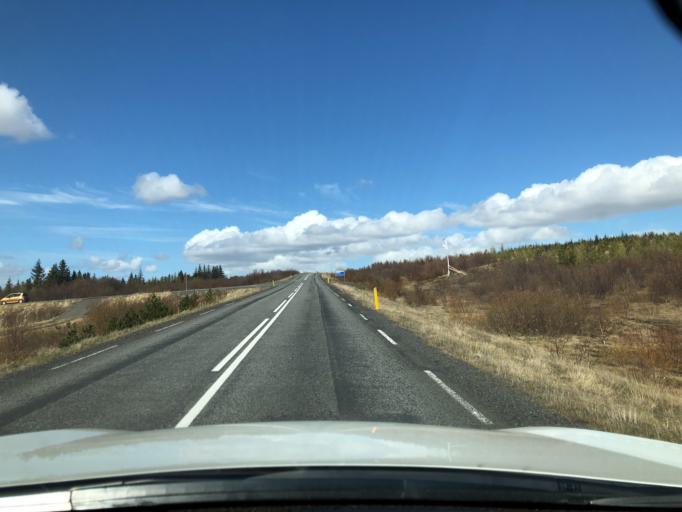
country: IS
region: West
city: Borgarnes
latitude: 64.6680
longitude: -21.4050
